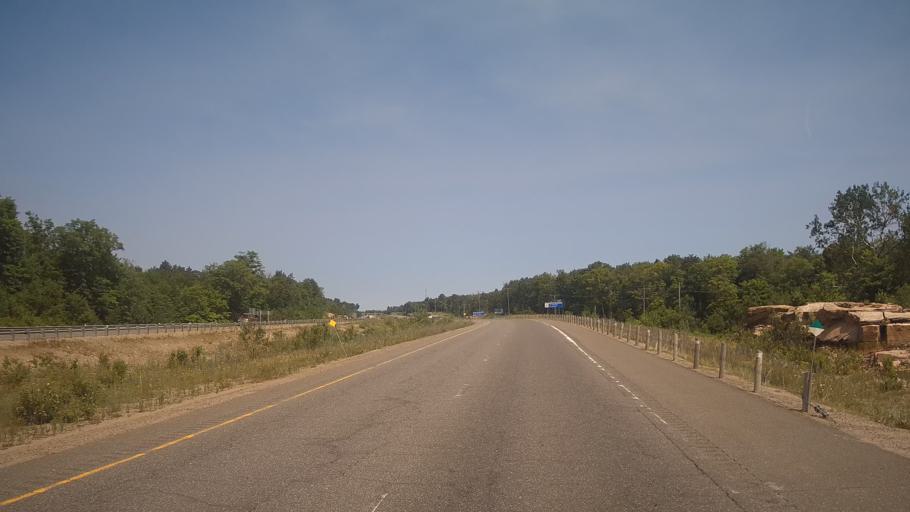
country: CA
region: Ontario
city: Midland
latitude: 45.0702
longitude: -79.7850
